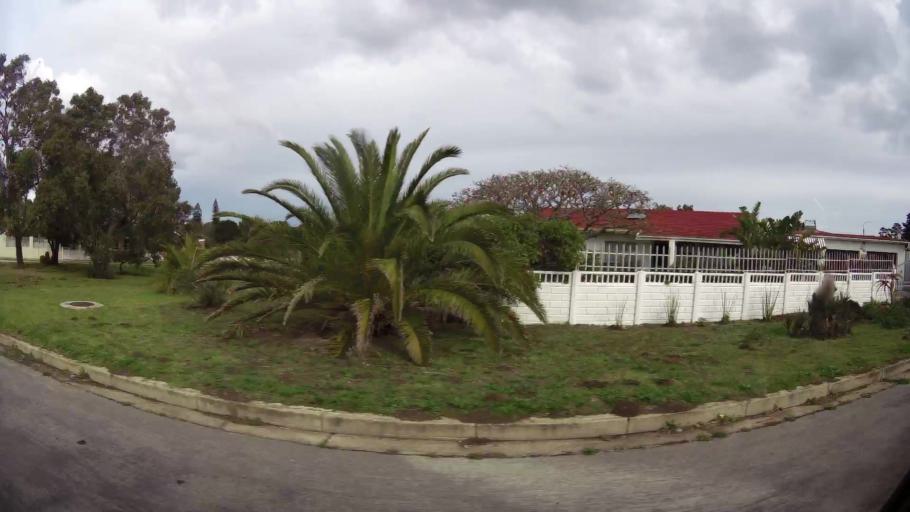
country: ZA
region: Eastern Cape
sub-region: Nelson Mandela Bay Metropolitan Municipality
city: Port Elizabeth
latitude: -33.9359
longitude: 25.5113
